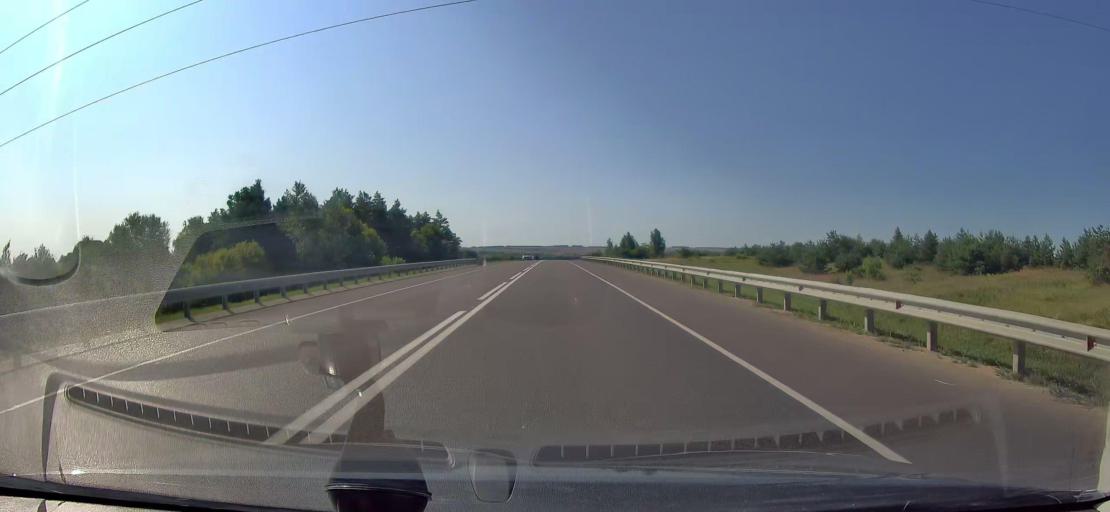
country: RU
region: Orjol
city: Kromy
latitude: 52.6811
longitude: 35.7040
